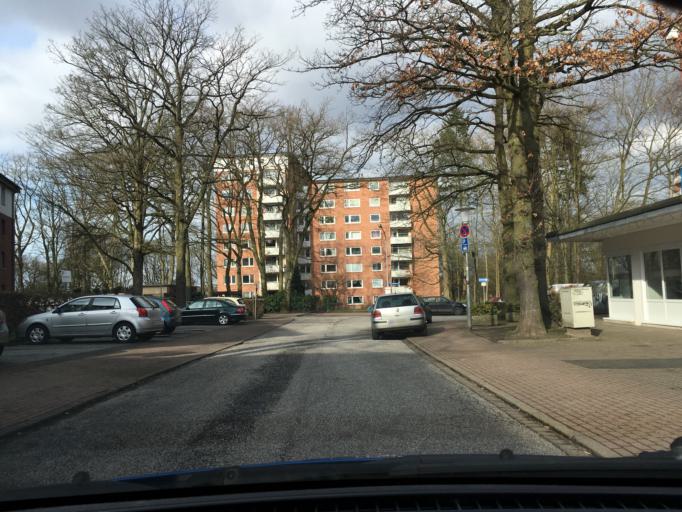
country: DE
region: Schleswig-Holstein
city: Wedel
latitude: 53.5836
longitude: 9.7155
